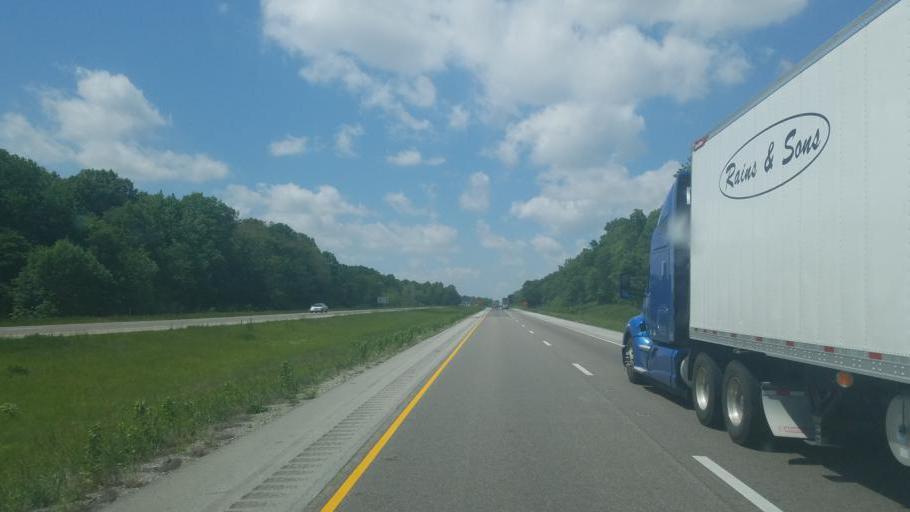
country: US
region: Illinois
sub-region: Cumberland County
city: Greenup
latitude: 39.2461
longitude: -88.1880
